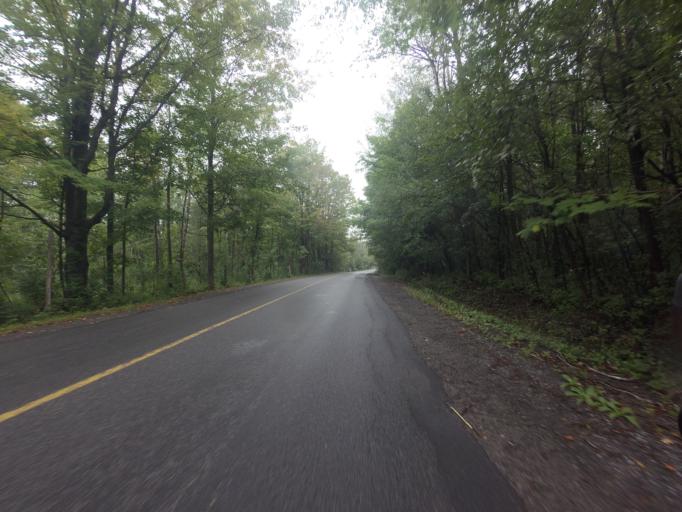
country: CA
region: Ontario
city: Bells Corners
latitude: 45.3423
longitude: -75.9720
